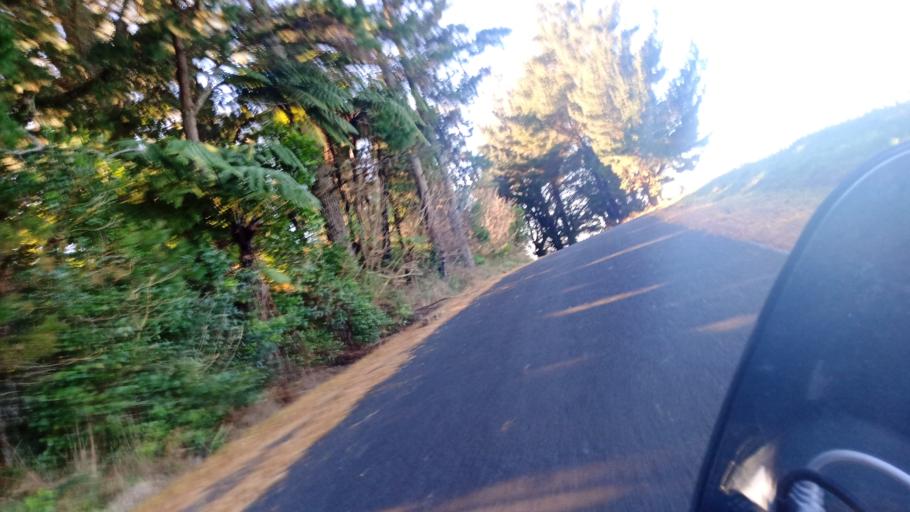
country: NZ
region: Hawke's Bay
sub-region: Wairoa District
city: Wairoa
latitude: -38.8327
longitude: 177.2670
